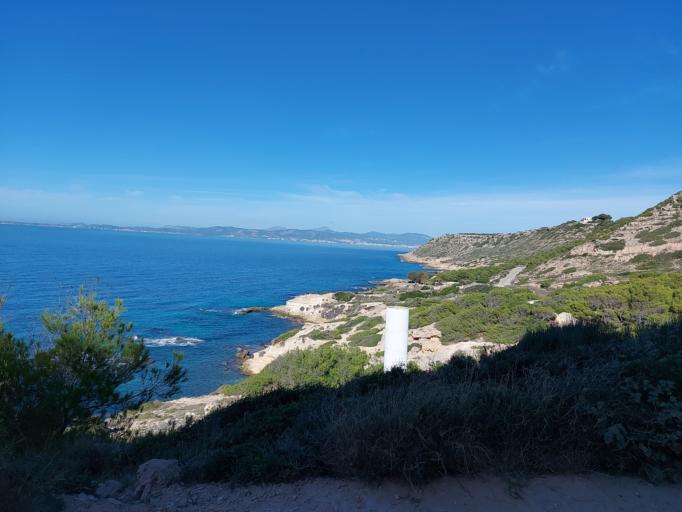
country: ES
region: Balearic Islands
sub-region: Illes Balears
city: s'Arenal
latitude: 39.4483
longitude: 2.7449
